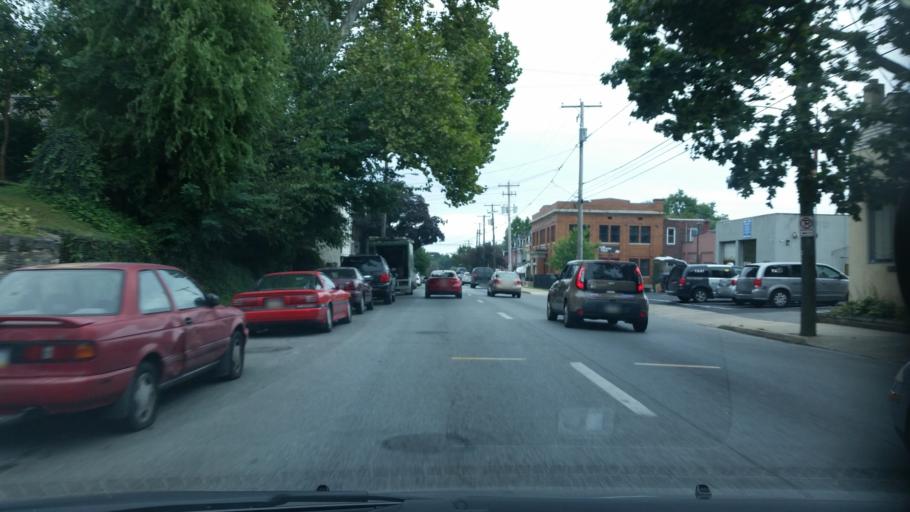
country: US
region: Pennsylvania
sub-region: Lancaster County
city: Lancaster
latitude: 40.0287
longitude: -76.3061
